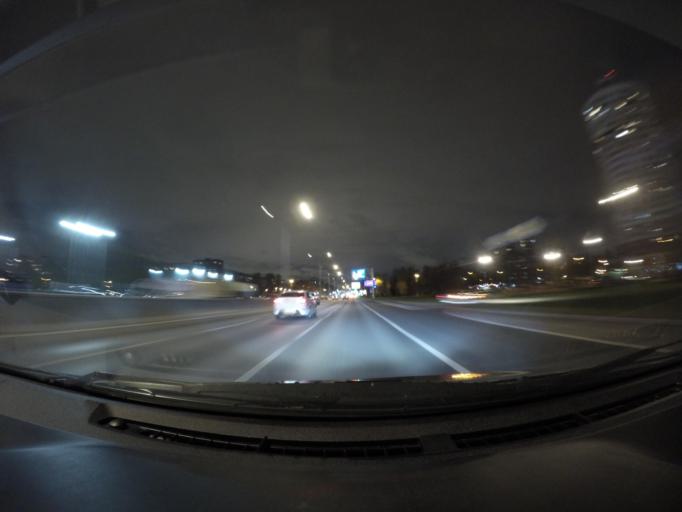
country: RU
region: Moscow
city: Vykhino-Zhulebino
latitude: 55.6947
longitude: 37.8116
